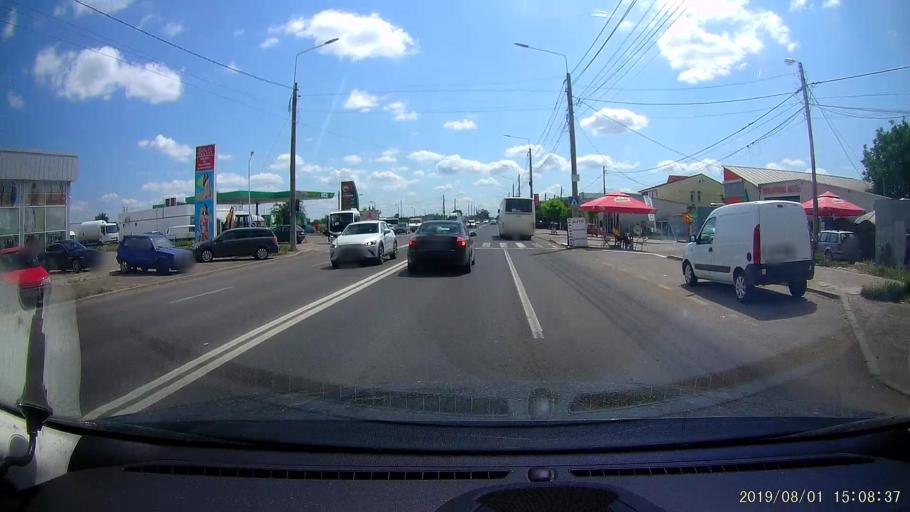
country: RO
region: Braila
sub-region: Municipiul Braila
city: Braila
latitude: 45.2399
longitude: 27.9440
